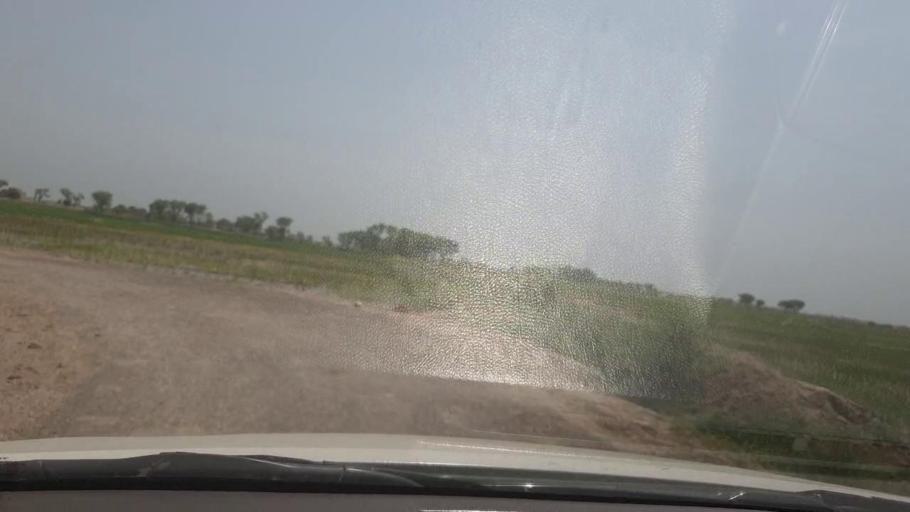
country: PK
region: Sindh
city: Shikarpur
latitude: 28.0444
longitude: 68.5710
